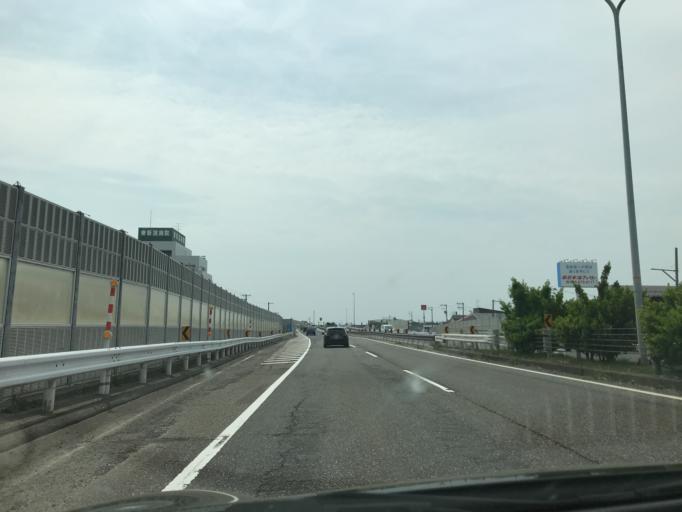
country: JP
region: Niigata
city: Kameda-honcho
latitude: 37.8858
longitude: 139.0784
